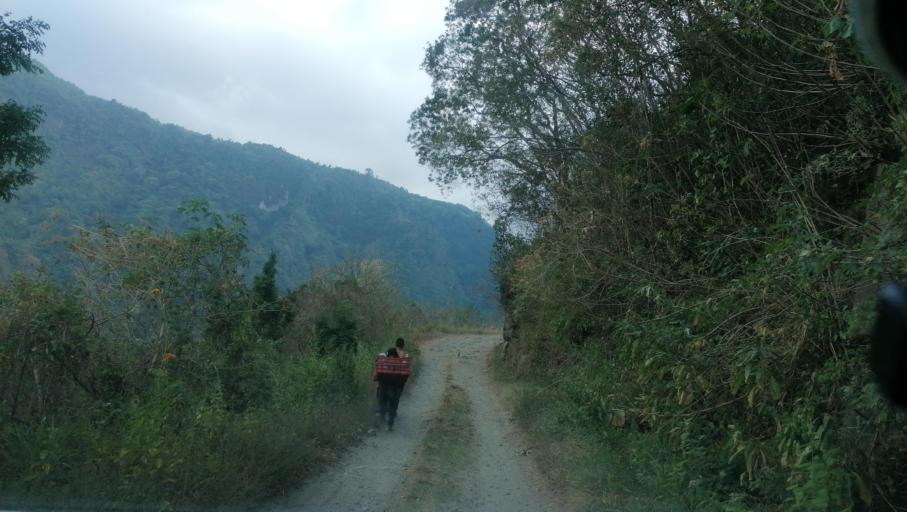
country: MX
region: Chiapas
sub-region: Cacahoatan
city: Benito Juarez
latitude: 15.1418
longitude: -92.1900
